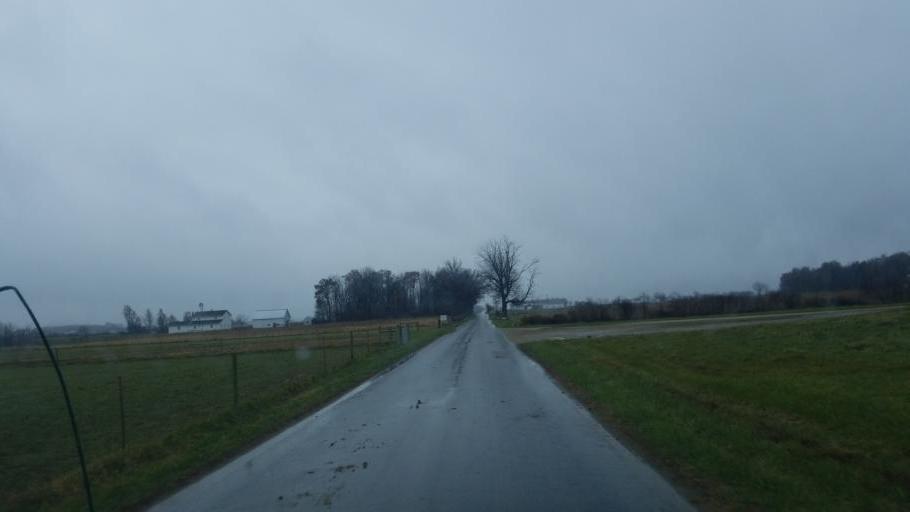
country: US
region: Indiana
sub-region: Adams County
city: Berne
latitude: 40.6269
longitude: -84.8784
